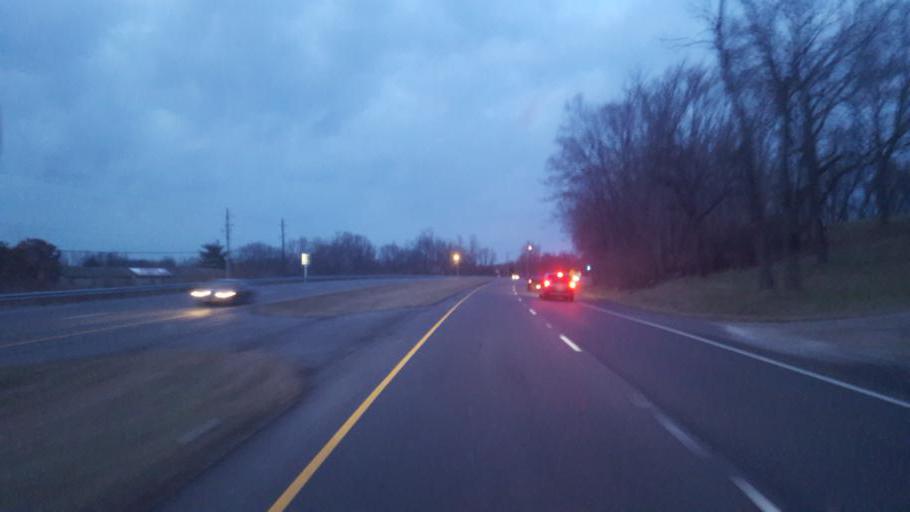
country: US
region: Ohio
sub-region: Ross County
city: Chillicothe
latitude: 39.3760
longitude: -82.9756
